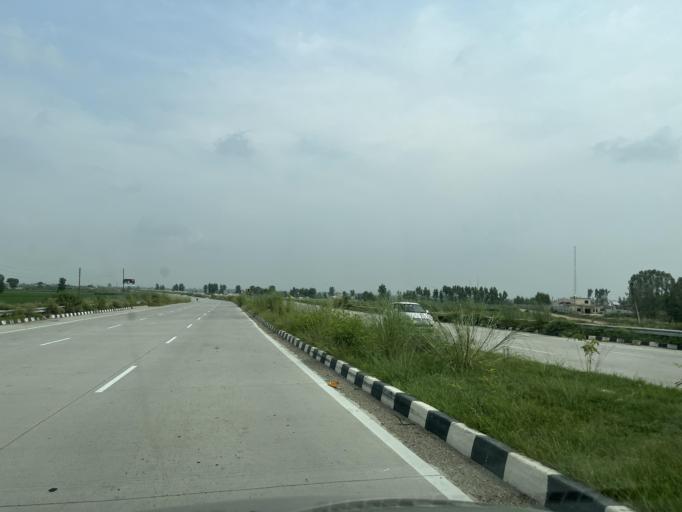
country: IN
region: Uttarakhand
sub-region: Udham Singh Nagar
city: Bazpur
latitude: 29.1496
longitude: 79.0245
